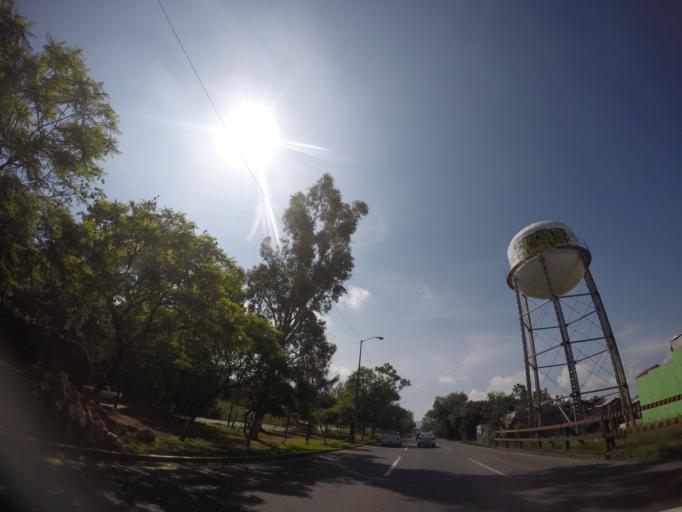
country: MX
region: Michoacan
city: Morelia
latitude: 19.7167
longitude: -101.1745
